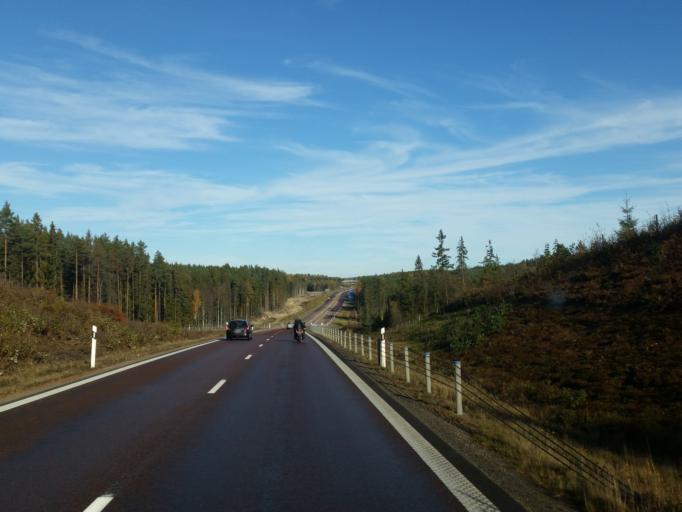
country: SE
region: Dalarna
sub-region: Faluns Kommun
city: Falun
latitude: 60.5609
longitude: 15.5860
